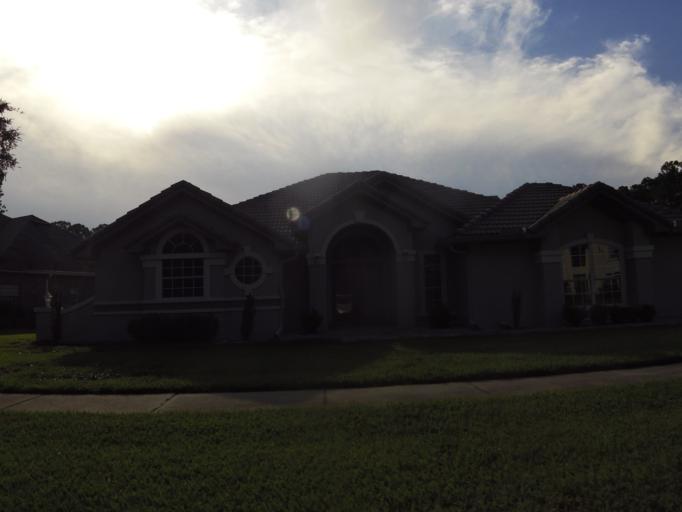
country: US
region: Florida
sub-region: Saint Johns County
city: Fruit Cove
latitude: 30.2075
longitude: -81.5367
